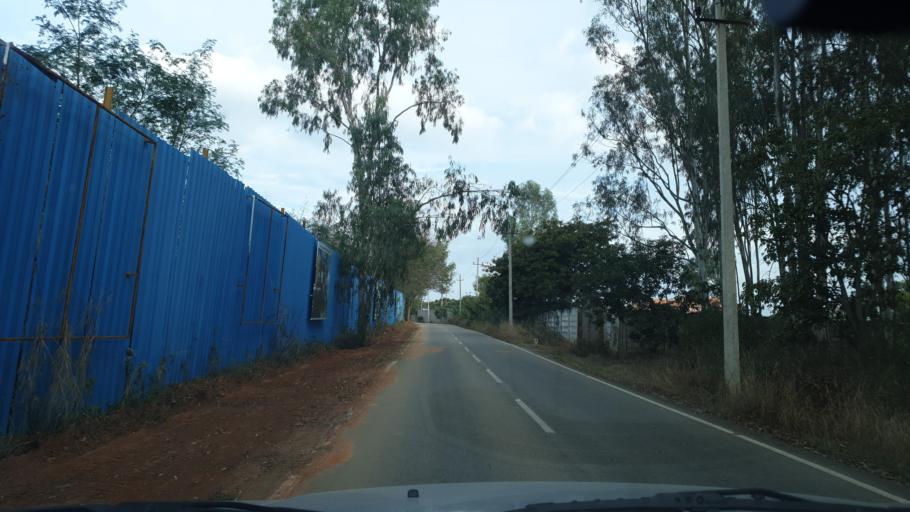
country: IN
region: Karnataka
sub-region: Bangalore Urban
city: Yelahanka
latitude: 13.2024
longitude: 77.6051
